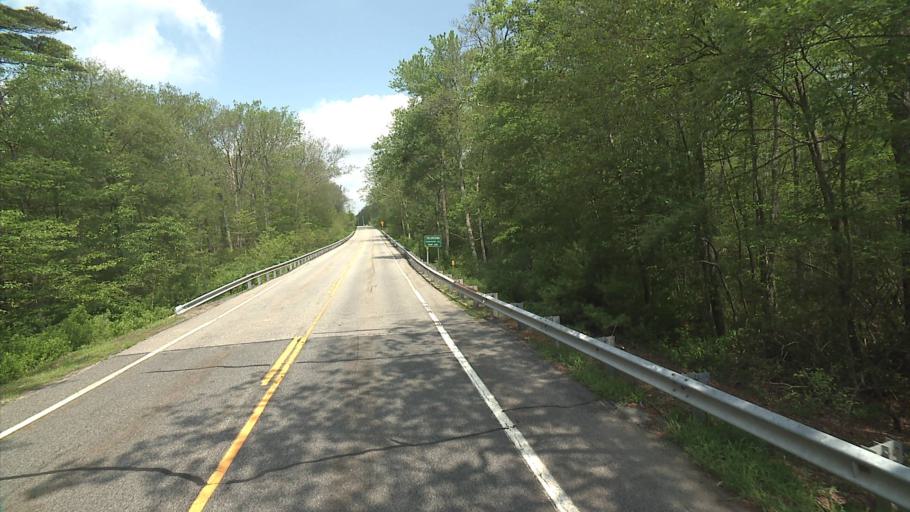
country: US
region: Rhode Island
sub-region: Washington County
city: Hope Valley
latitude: 41.5529
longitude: -71.7910
